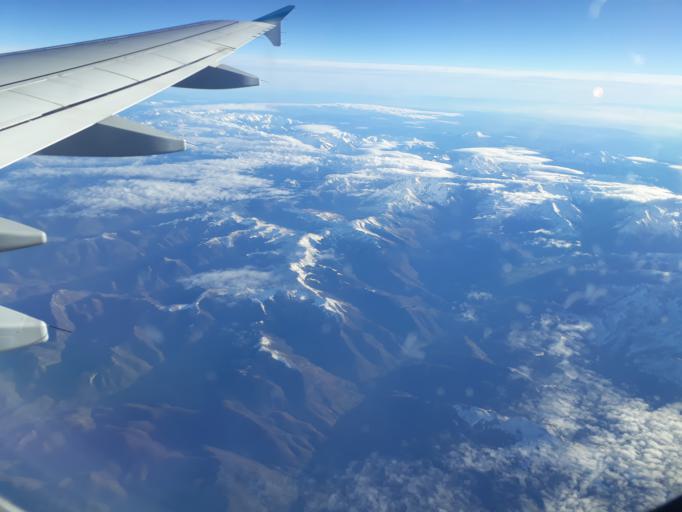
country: FR
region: Midi-Pyrenees
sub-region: Departement des Hautes-Pyrenees
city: Capvern
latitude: 43.0971
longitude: 0.3111
